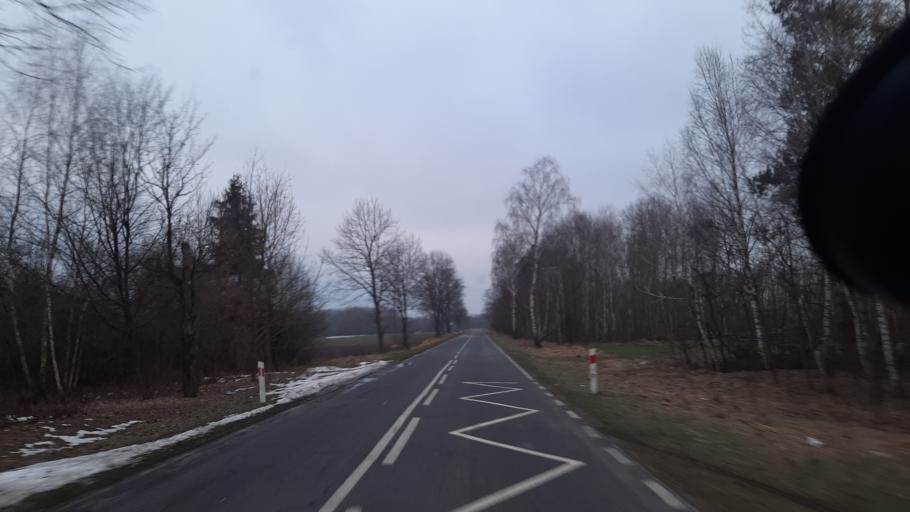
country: PL
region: Lublin Voivodeship
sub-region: Powiat parczewski
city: Podedworze
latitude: 51.5963
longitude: 23.1592
